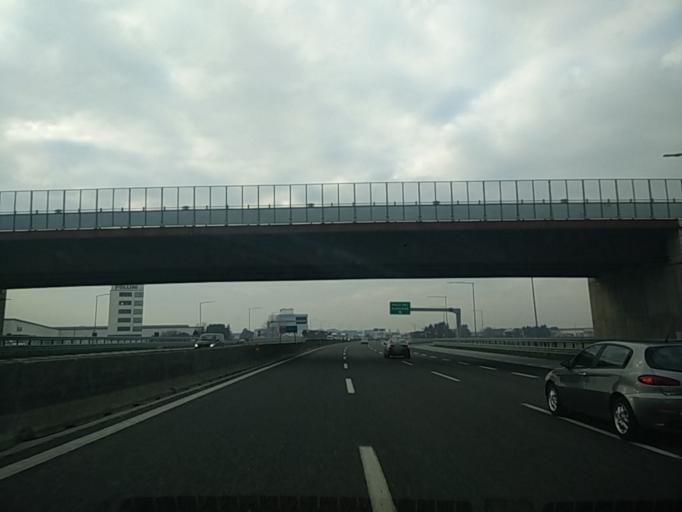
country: IT
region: Emilia-Romagna
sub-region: Forli-Cesena
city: Gatteo-Sant'Angelo
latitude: 44.1197
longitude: 12.3940
